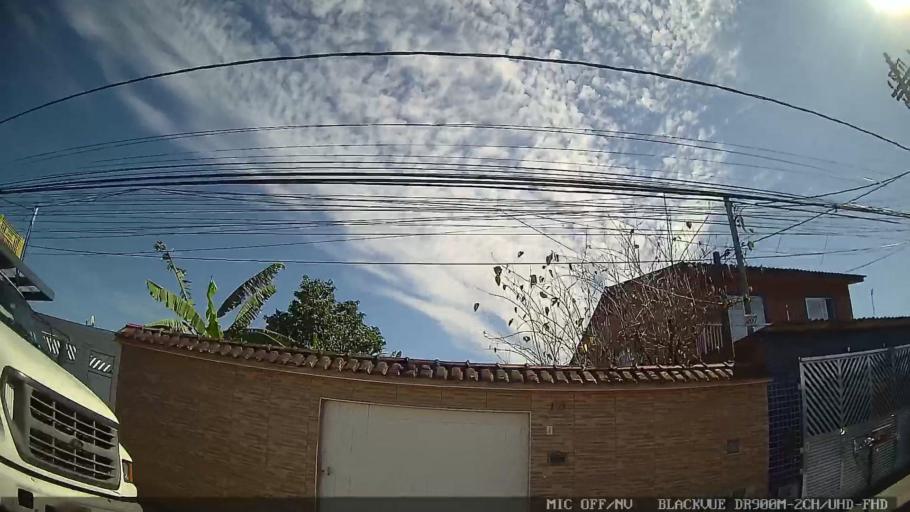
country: BR
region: Sao Paulo
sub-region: Guaruja
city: Guaruja
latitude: -23.9505
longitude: -46.2797
